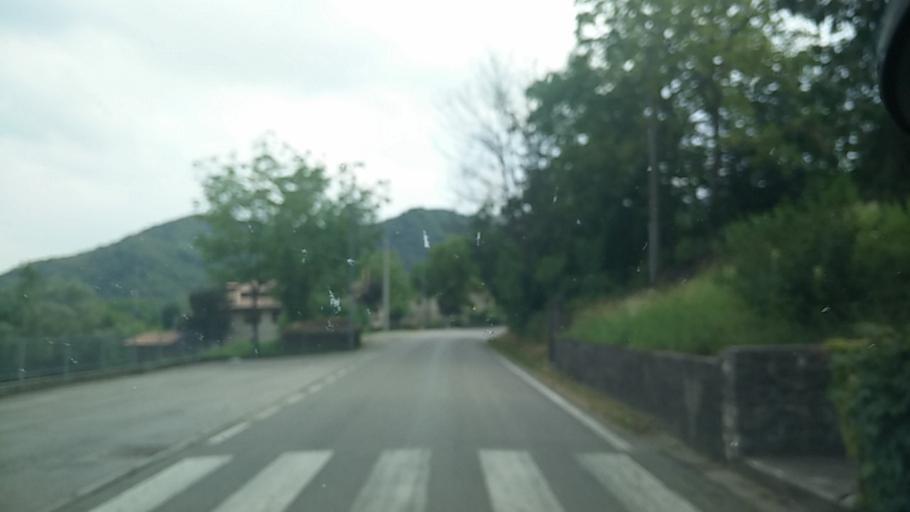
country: IT
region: Veneto
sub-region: Provincia di Treviso
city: Follina
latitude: 45.9358
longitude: 12.1260
